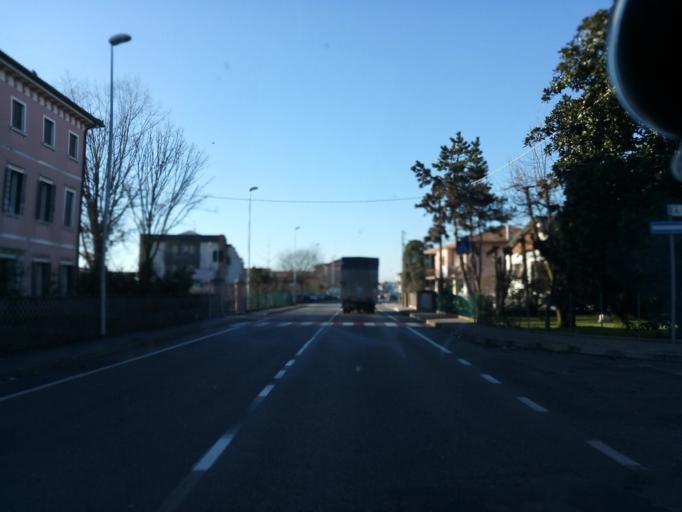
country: IT
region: Veneto
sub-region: Provincia di Padova
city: Piombino Dese
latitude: 45.6077
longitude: 11.9950
